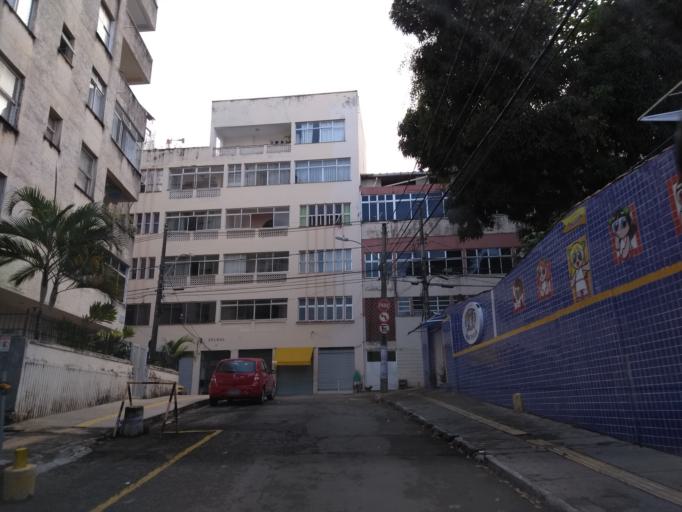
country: BR
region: Bahia
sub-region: Salvador
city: Salvador
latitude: -13.0043
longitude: -38.5255
